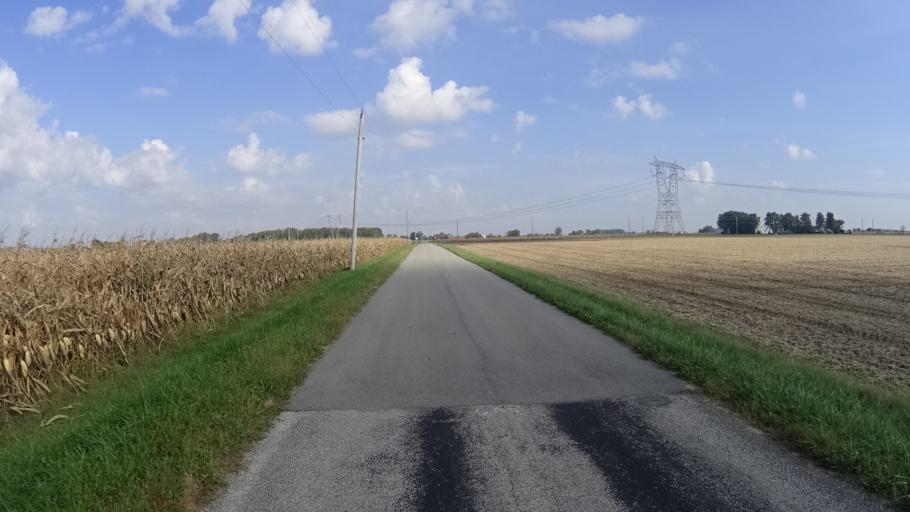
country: US
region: Indiana
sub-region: Madison County
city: Ingalls
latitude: 40.0001
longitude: -85.8245
